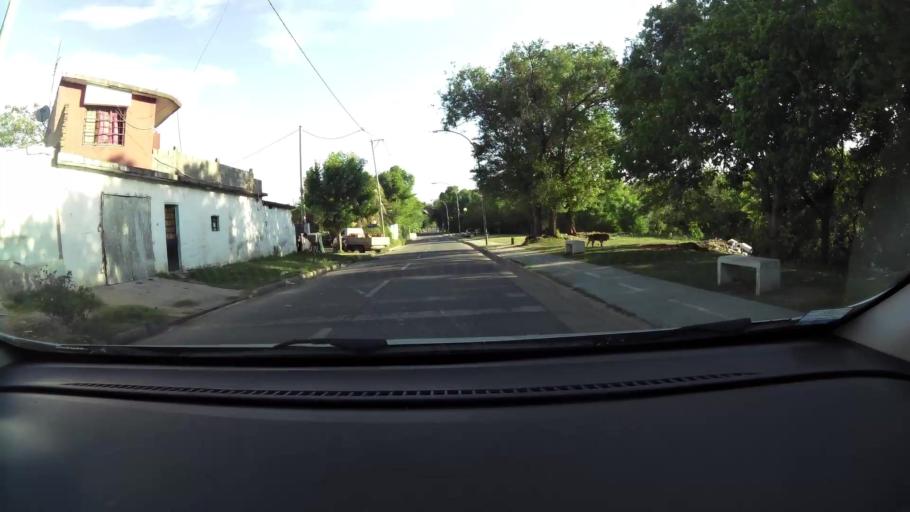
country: AR
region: Cordoba
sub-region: Departamento de Capital
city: Cordoba
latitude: -31.3779
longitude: -64.2490
